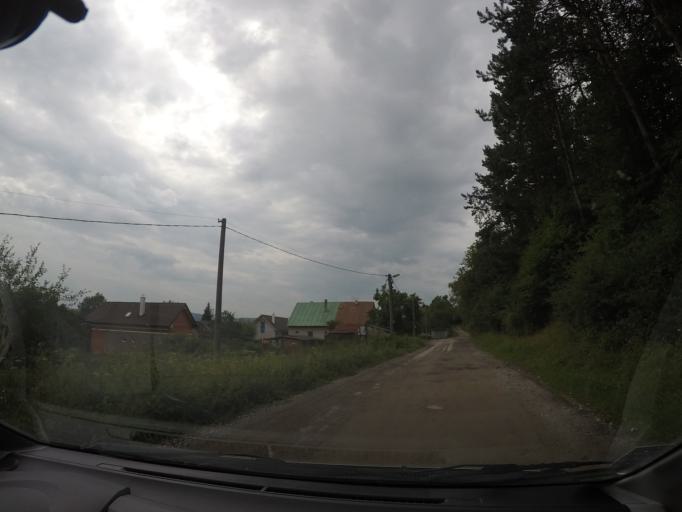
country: SK
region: Nitriansky
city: Bojnice
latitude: 48.9058
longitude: 18.6036
